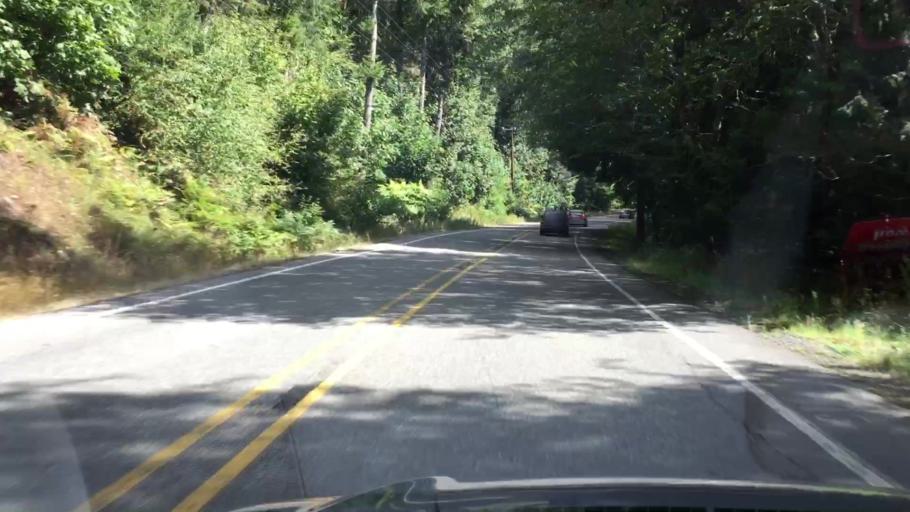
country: US
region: Washington
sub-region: Pierce County
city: Eatonville
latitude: 46.7547
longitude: -121.9461
